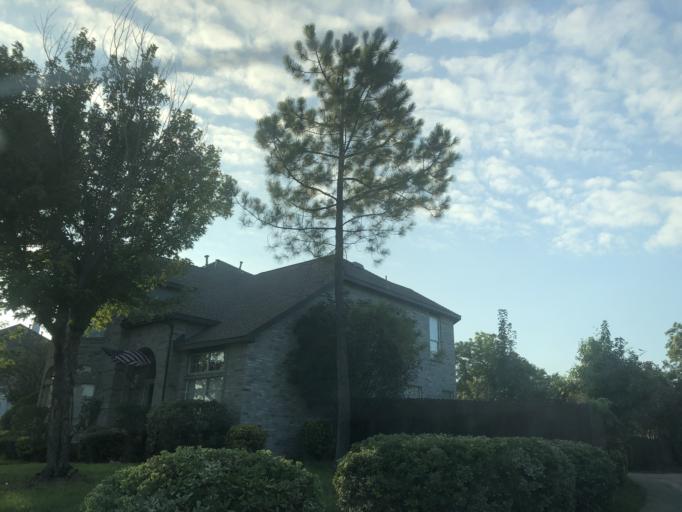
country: US
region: Texas
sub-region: Dallas County
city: Sunnyvale
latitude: 32.8406
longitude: -96.5619
